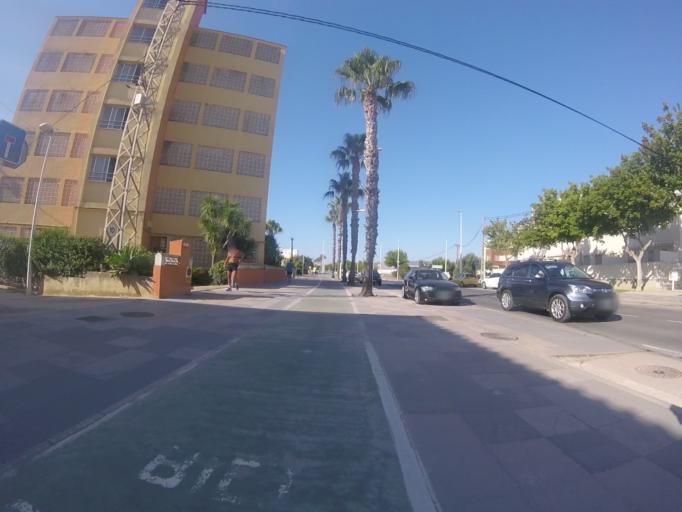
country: ES
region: Valencia
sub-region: Provincia de Castello
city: Benicarlo
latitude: 40.4045
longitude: 0.4199
